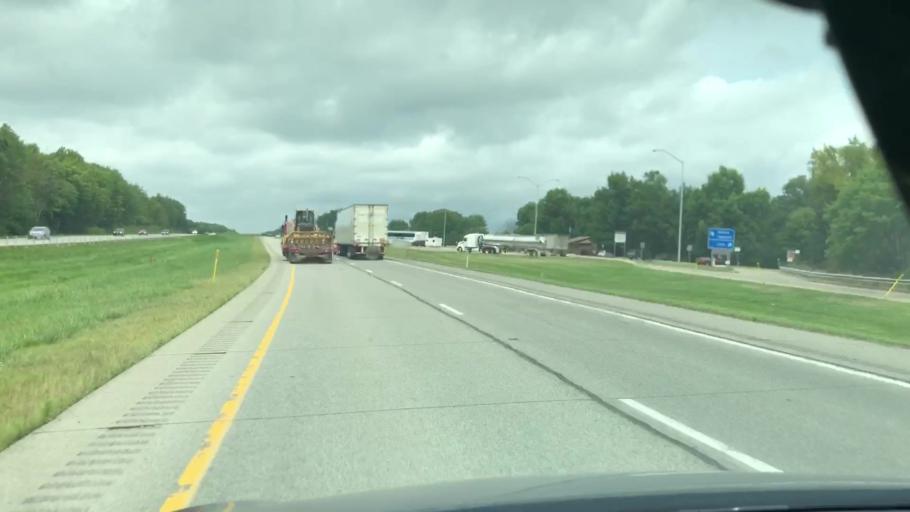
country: US
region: Pennsylvania
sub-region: Butler County
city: Slippery Rock
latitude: 41.0688
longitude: -80.1239
